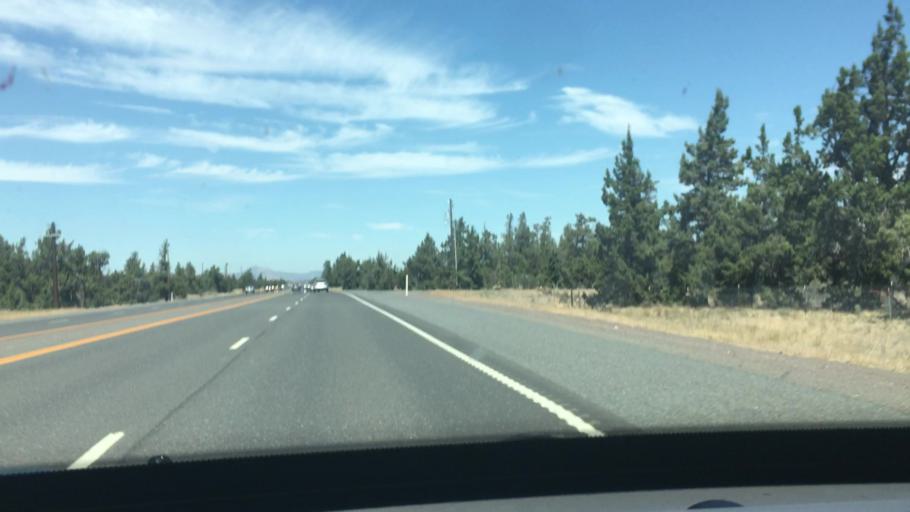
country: US
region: Oregon
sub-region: Deschutes County
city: Bend
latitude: 44.1420
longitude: -121.2718
